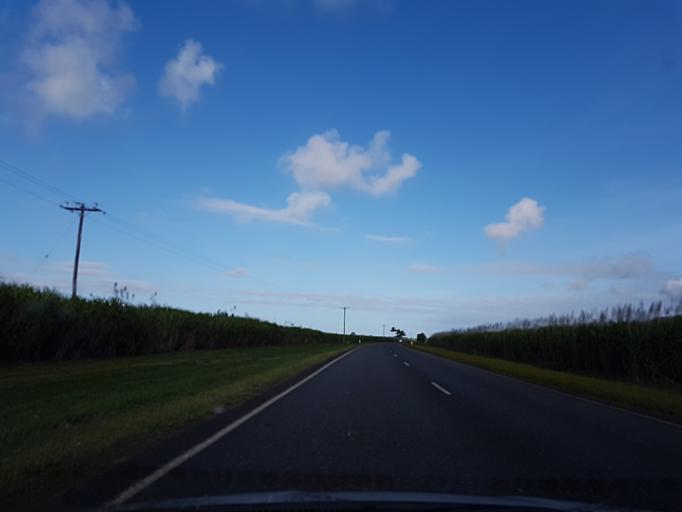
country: AU
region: Queensland
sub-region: Cairns
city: Port Douglas
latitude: -16.2873
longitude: 145.3831
